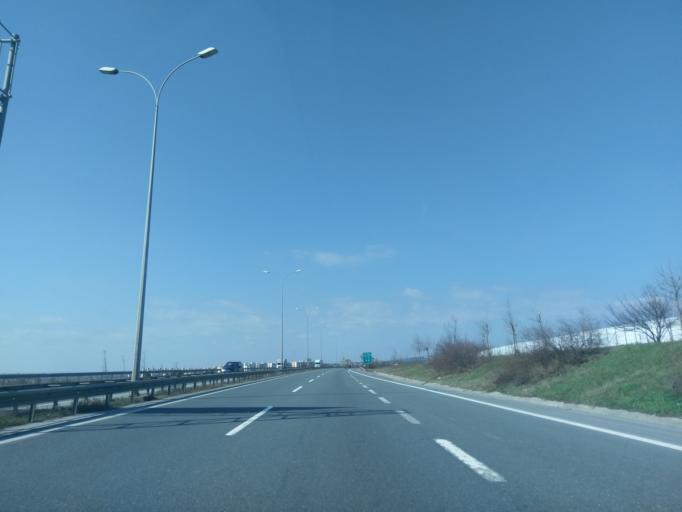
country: TR
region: Istanbul
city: Selimpasa
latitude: 41.0721
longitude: 28.3807
